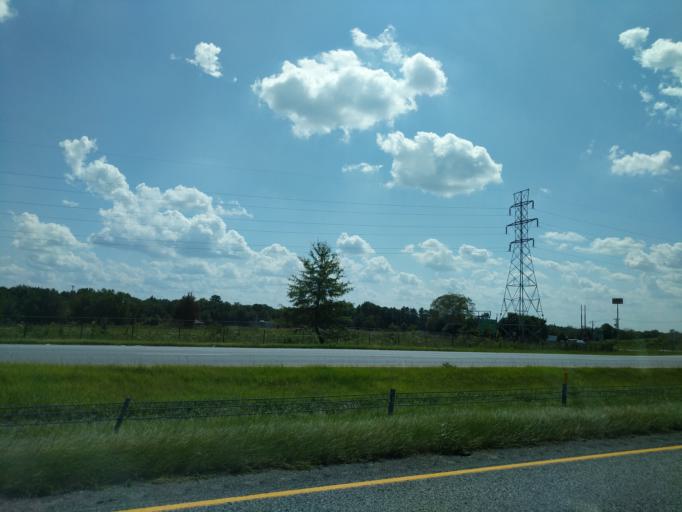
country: US
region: South Carolina
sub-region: Spartanburg County
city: Arcadia
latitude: 34.9704
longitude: -81.9975
